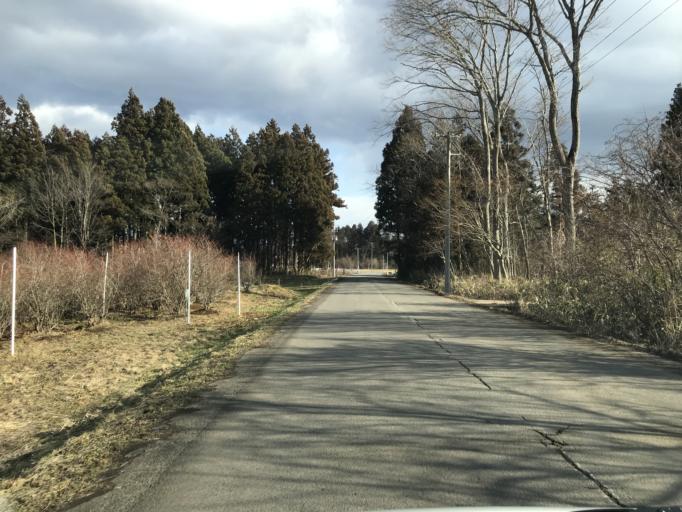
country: JP
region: Iwate
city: Mizusawa
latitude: 39.0982
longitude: 141.0307
